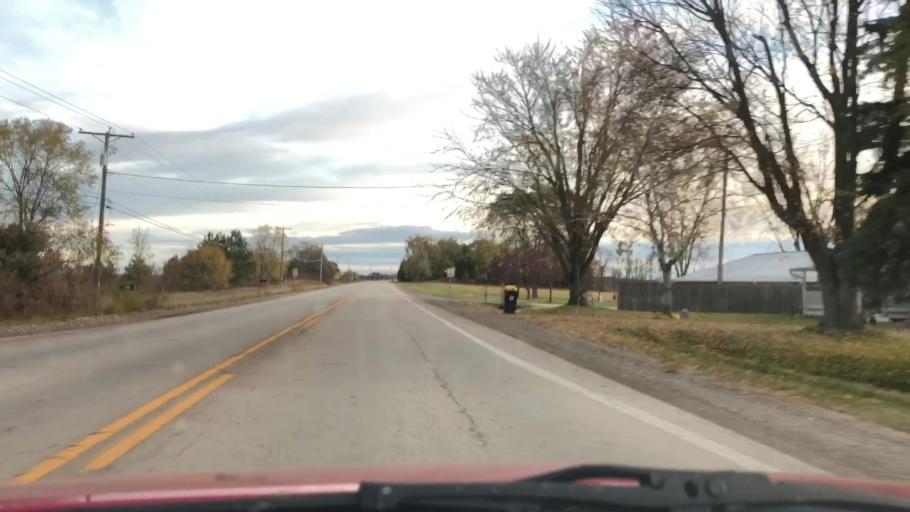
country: US
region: Wisconsin
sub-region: Brown County
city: Oneida
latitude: 44.4161
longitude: -88.2552
